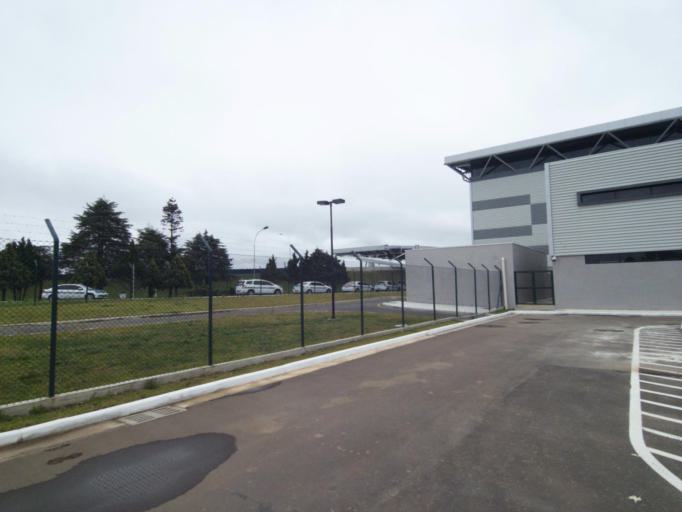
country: BR
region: Parana
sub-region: Sao Jose Dos Pinhais
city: Sao Jose dos Pinhais
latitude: -25.5374
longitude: -49.1722
